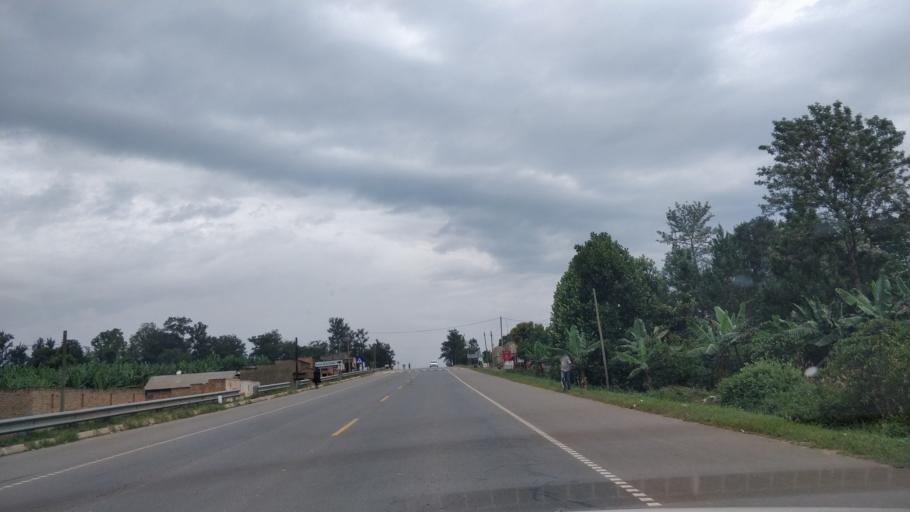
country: UG
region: Western Region
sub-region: Sheema District
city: Kibingo
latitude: -0.6589
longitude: 30.4631
